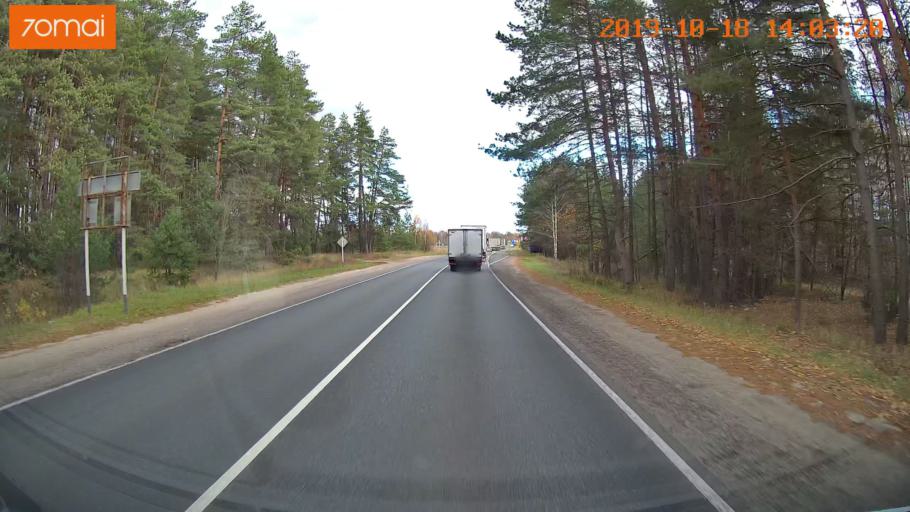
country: RU
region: Rjazan
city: Spas-Klepiki
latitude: 55.1170
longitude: 40.1243
